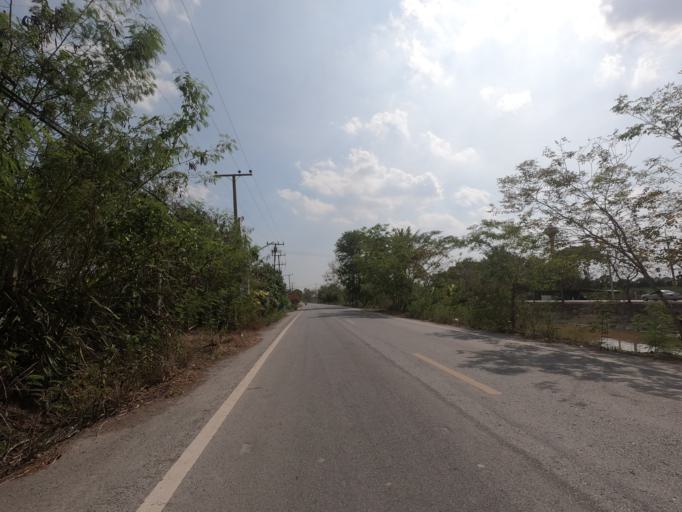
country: TH
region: Pathum Thani
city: Nong Suea
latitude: 14.1489
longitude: 100.8464
